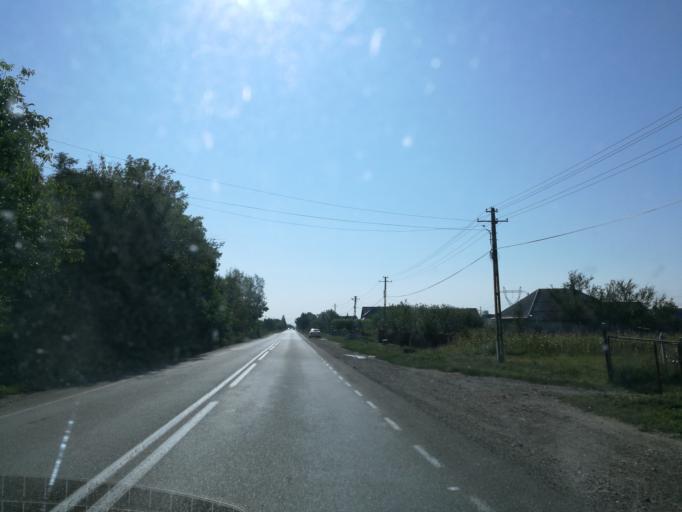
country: RO
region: Neamt
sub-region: Comuna Draganesti
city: Draganesti
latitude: 47.3546
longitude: 26.4062
